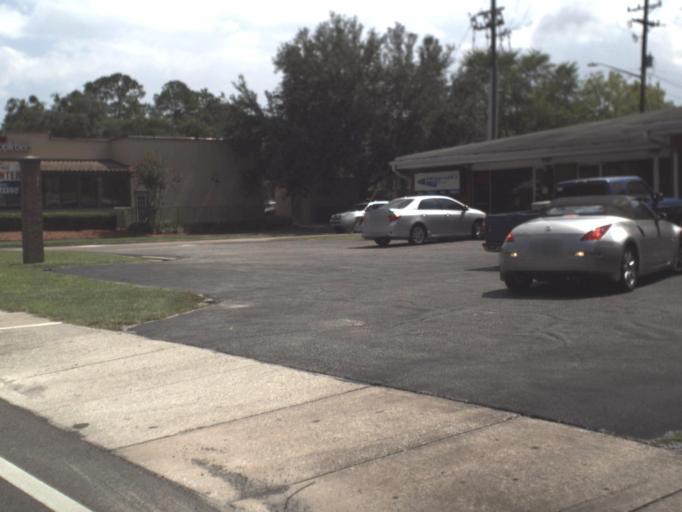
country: US
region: Florida
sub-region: Alachua County
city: Gainesville
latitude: 29.6608
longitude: -82.3391
